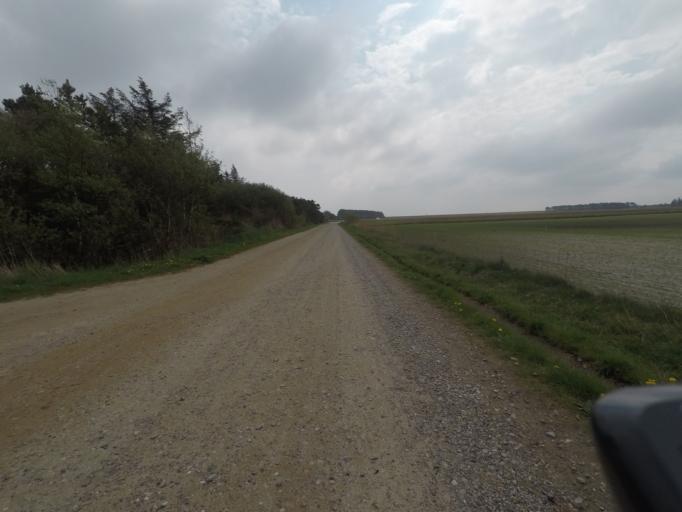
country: DE
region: Schleswig-Holstein
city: List
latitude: 55.0863
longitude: 8.5265
